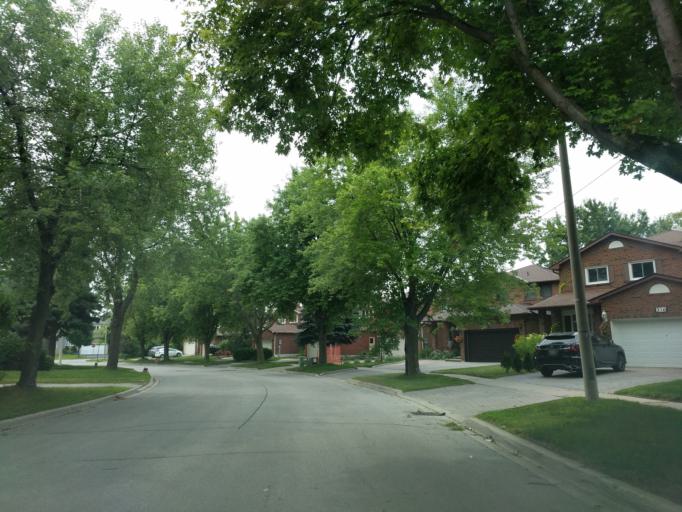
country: CA
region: Ontario
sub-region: York
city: Richmond Hill
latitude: 43.8685
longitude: -79.4193
